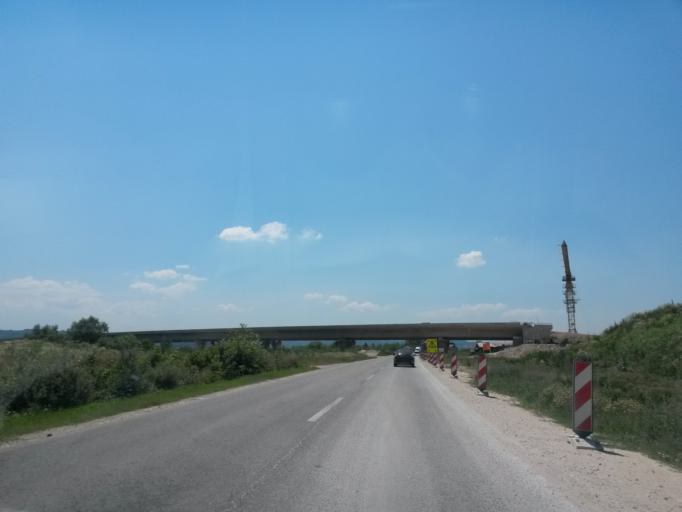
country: BA
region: Republika Srpska
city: Doboj
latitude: 44.8080
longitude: 18.0527
